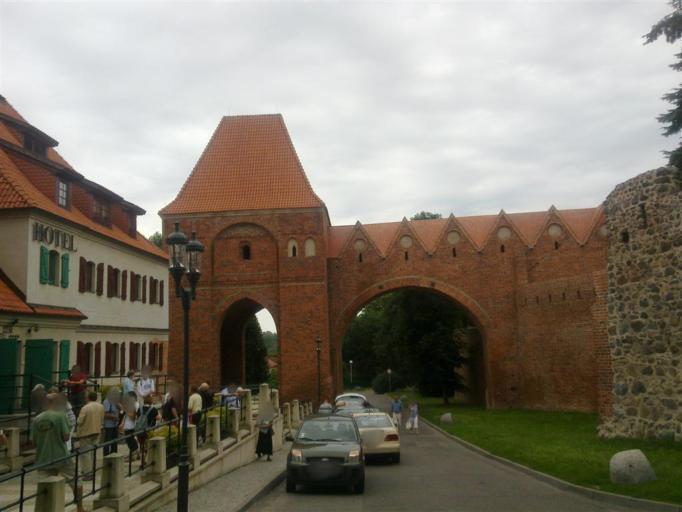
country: PL
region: Kujawsko-Pomorskie
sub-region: Torun
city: Torun
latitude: 53.0099
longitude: 18.6107
